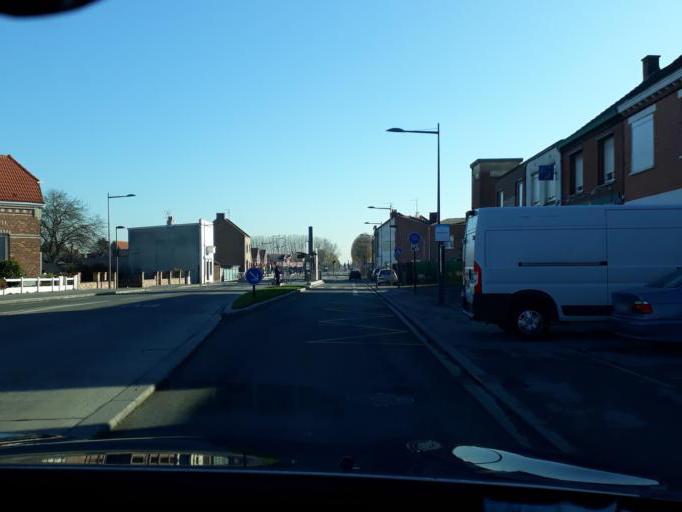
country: FR
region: Nord-Pas-de-Calais
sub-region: Departement du Nord
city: Lewarde
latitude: 50.3388
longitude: 3.1857
